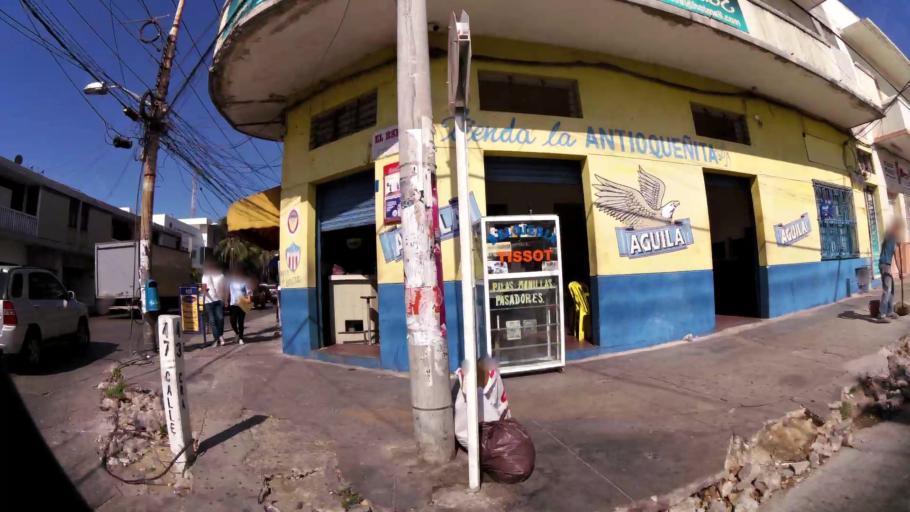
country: CO
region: Atlantico
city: Barranquilla
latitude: 10.9833
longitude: -74.7873
